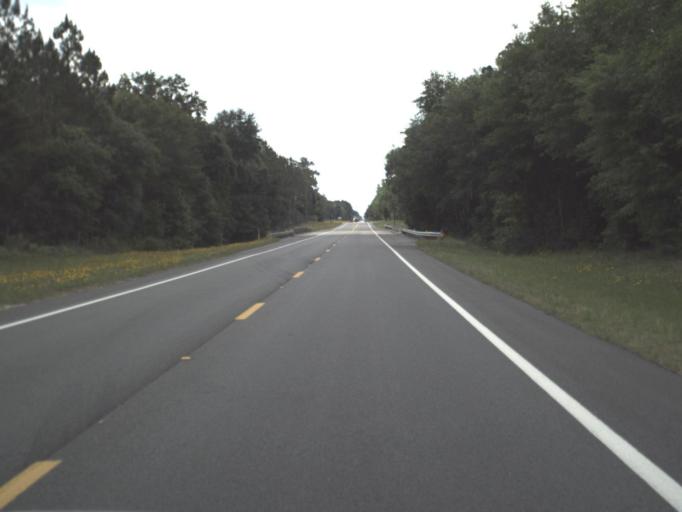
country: US
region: Florida
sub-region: Columbia County
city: Five Points
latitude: 30.4082
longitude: -82.6345
